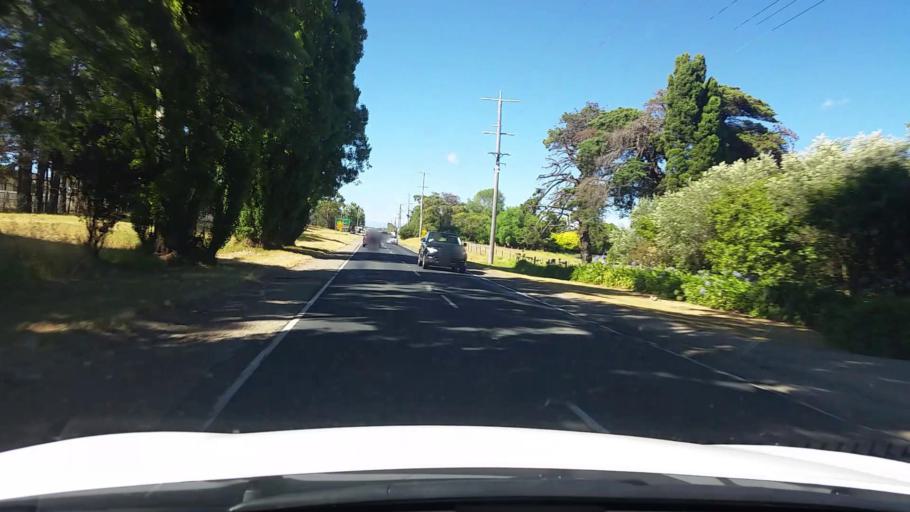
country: AU
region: Victoria
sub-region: Mornington Peninsula
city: Rosebud West
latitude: -38.3952
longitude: 144.8882
